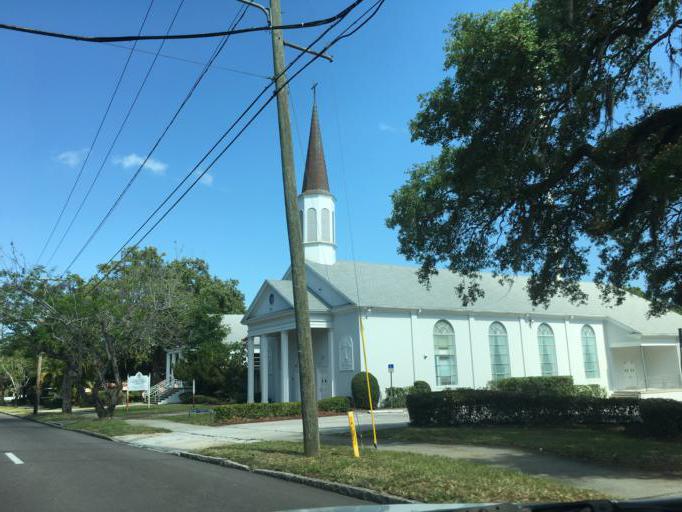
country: US
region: Florida
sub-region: Pinellas County
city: Saint Petersburg
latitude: 27.7484
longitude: -82.6532
